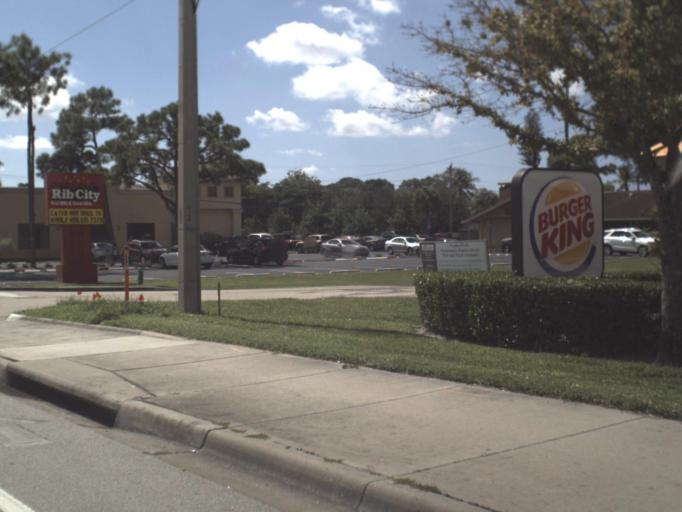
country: US
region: Florida
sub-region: Collier County
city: Naples Park
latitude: 26.2556
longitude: -81.8014
